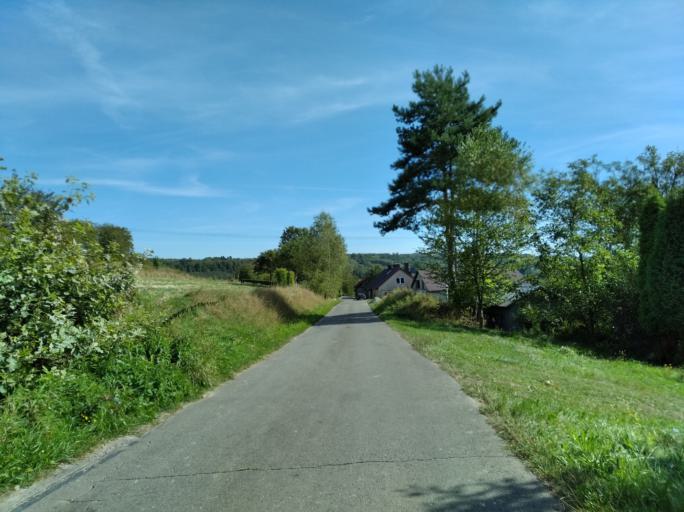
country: PL
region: Subcarpathian Voivodeship
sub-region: Powiat strzyzowski
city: Wisniowa
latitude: 49.8955
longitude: 21.6353
